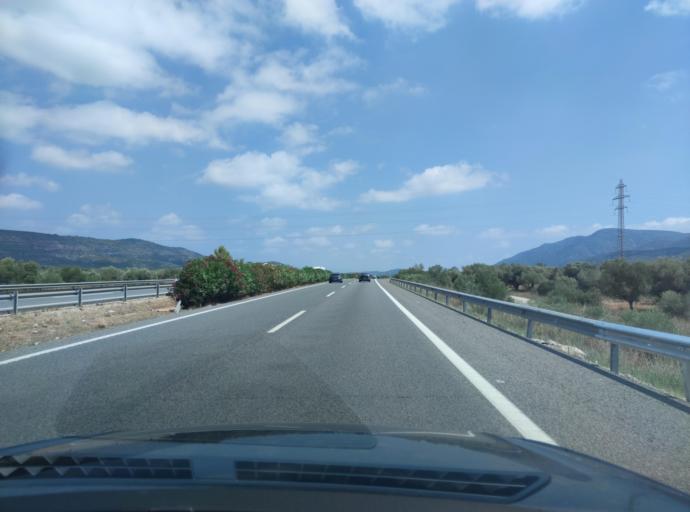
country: ES
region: Catalonia
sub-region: Provincia de Tarragona
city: Ulldecona
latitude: 40.6140
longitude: 0.4795
